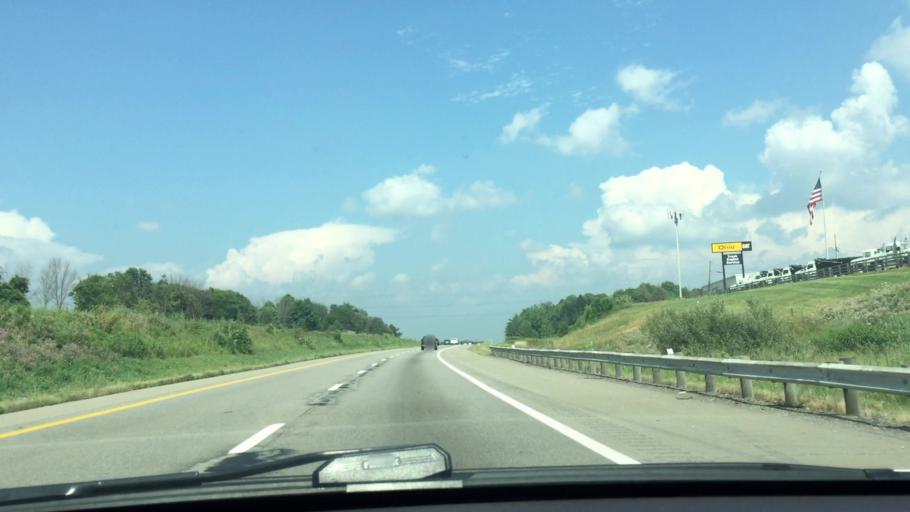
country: US
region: Ohio
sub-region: Muskingum County
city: Pleasant Grove
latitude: 39.9554
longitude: -81.9438
